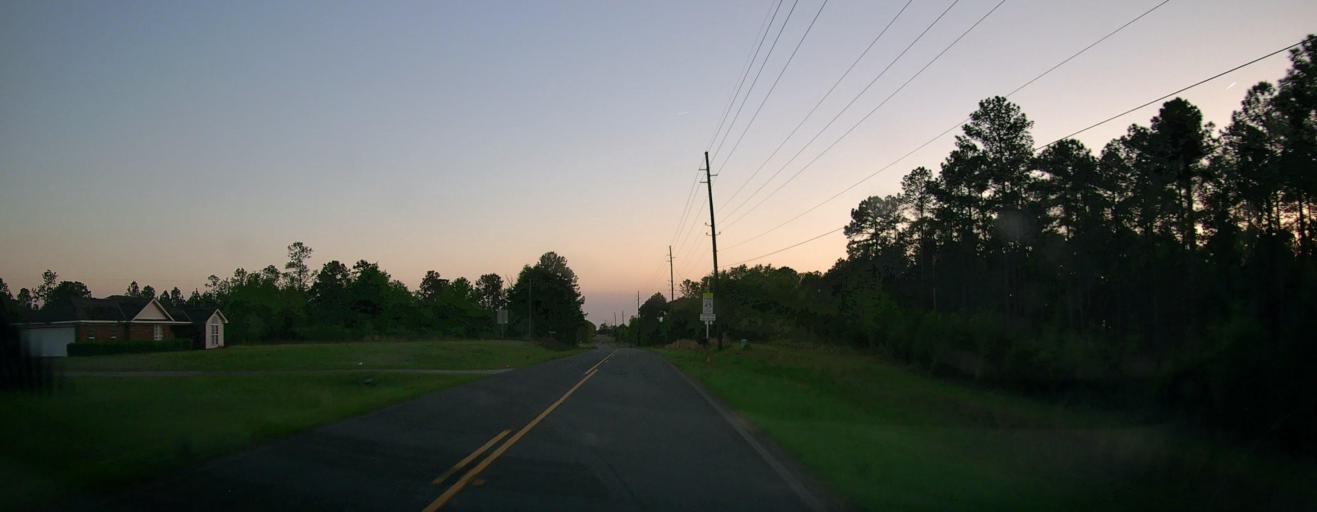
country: US
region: Georgia
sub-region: Marion County
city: Buena Vista
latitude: 32.2907
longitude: -84.5341
